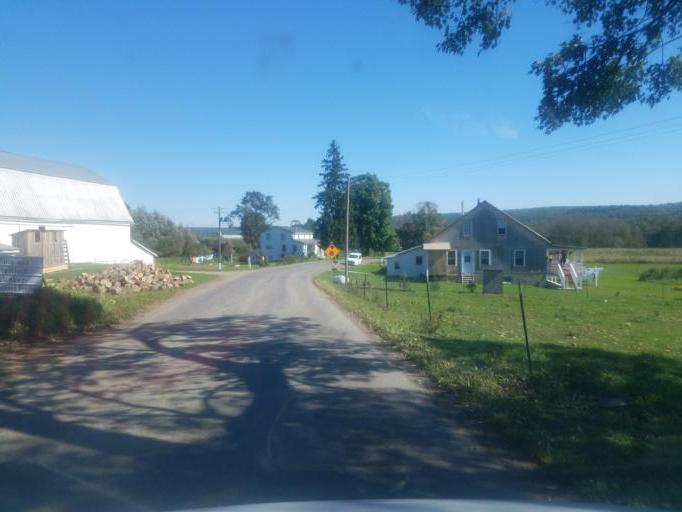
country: US
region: New York
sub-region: Allegany County
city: Friendship
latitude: 42.3005
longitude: -78.1905
